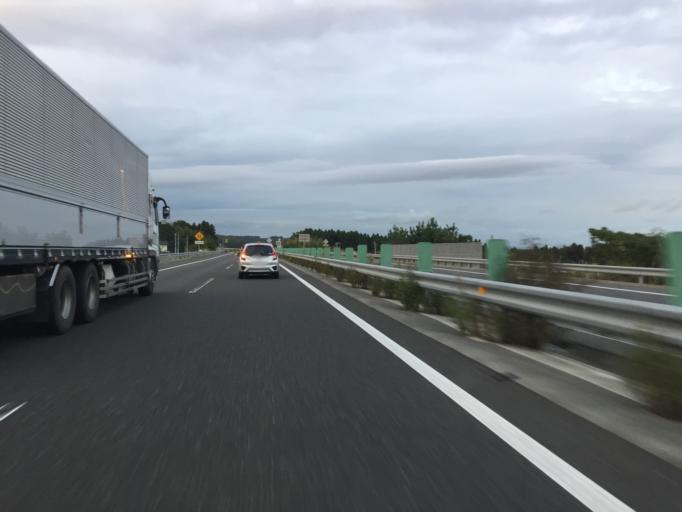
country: JP
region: Miyagi
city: Marumori
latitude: 37.7657
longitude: 140.9015
